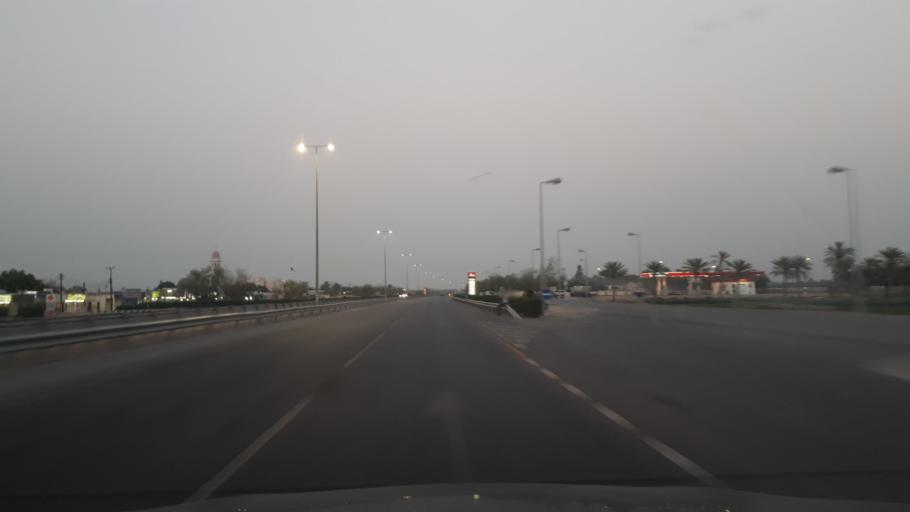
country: OM
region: Al Batinah
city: Barka'
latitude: 23.7352
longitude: 57.6758
